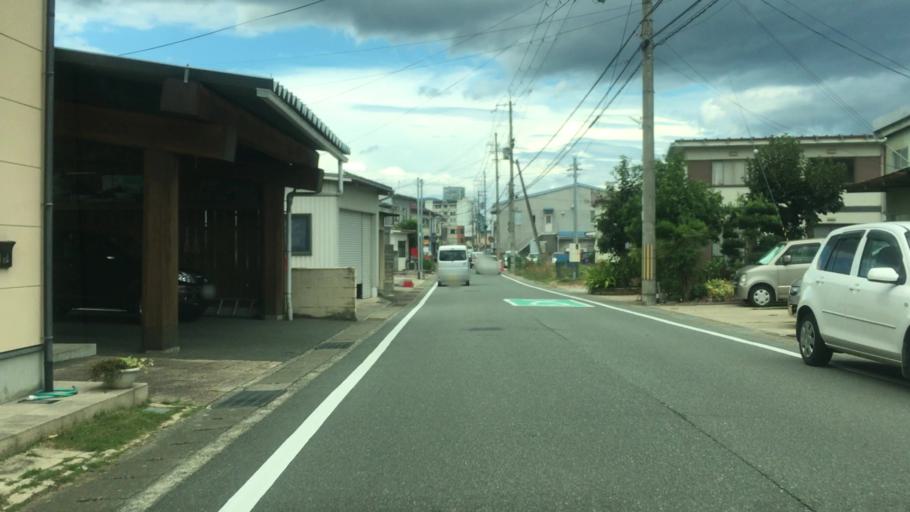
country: JP
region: Hyogo
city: Toyooka
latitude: 35.5294
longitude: 134.8220
